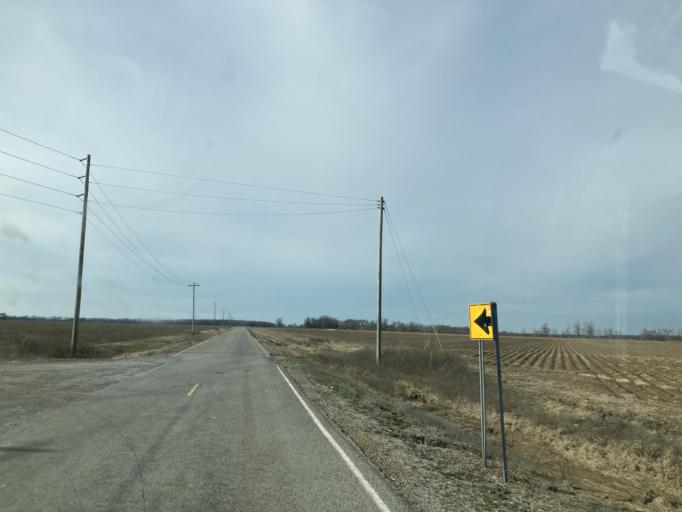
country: US
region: Mississippi
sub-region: Humphreys County
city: Belzoni
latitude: 33.0634
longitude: -90.6296
